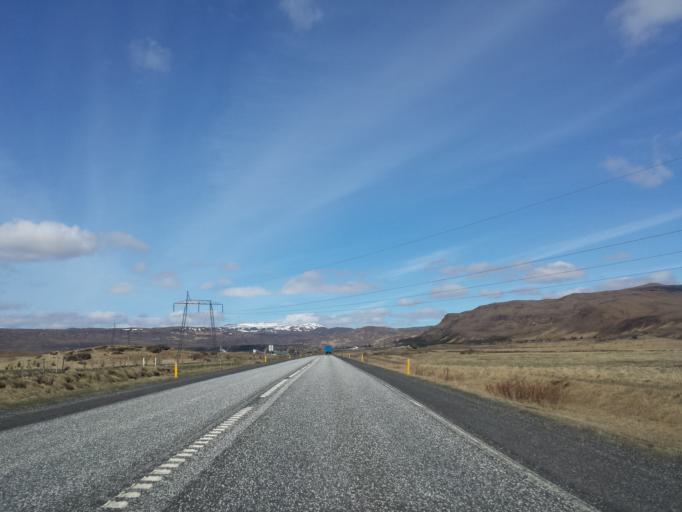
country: IS
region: South
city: Hveragerdi
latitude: 63.9811
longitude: -21.1534
